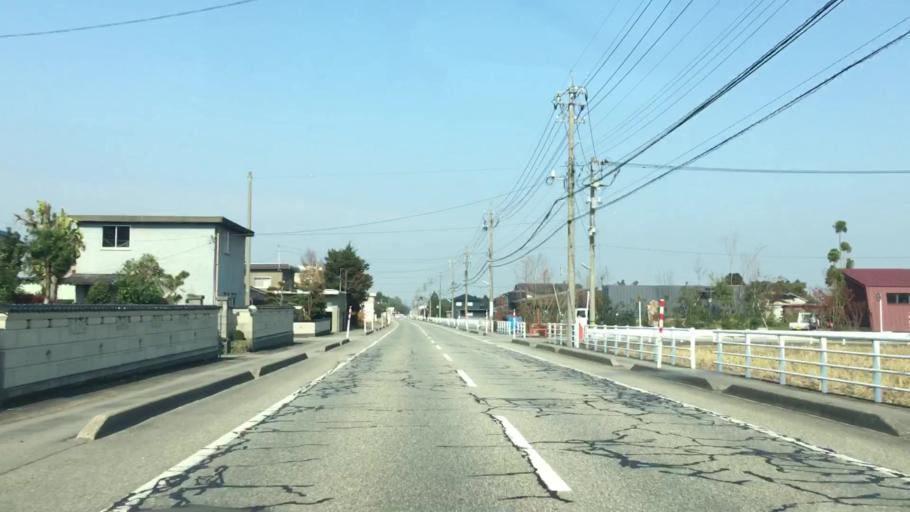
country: JP
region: Toyama
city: Yatsuomachi-higashikumisaka
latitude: 36.5828
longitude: 137.1921
